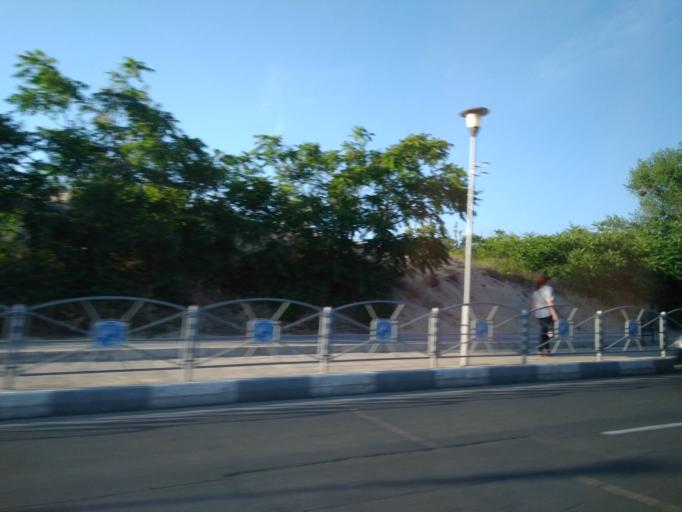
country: BG
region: Burgas
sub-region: Obshtina Nesebur
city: Nesebar
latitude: 42.6652
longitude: 27.7103
